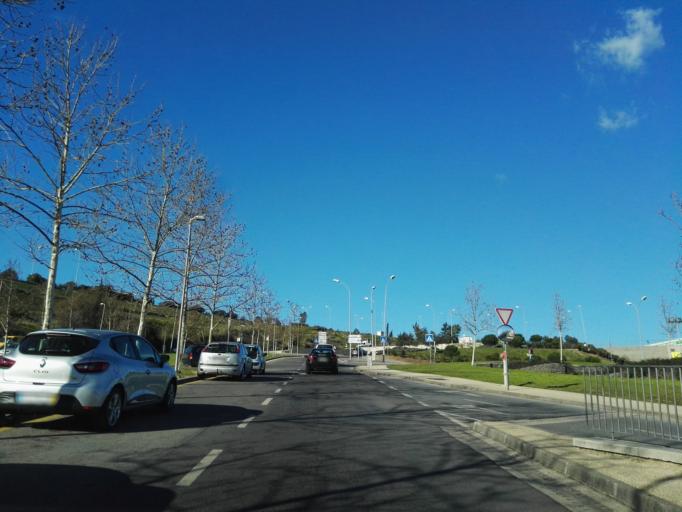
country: PT
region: Lisbon
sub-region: Odivelas
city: Famoes
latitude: 38.7784
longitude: -9.2207
